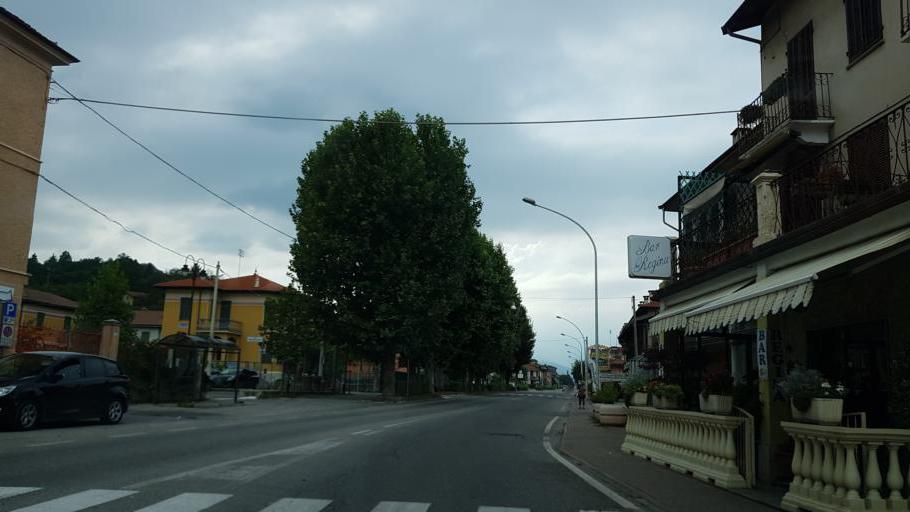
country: IT
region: Piedmont
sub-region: Provincia di Cuneo
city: Borgo San Dalmazzo
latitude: 44.3302
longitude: 7.4841
